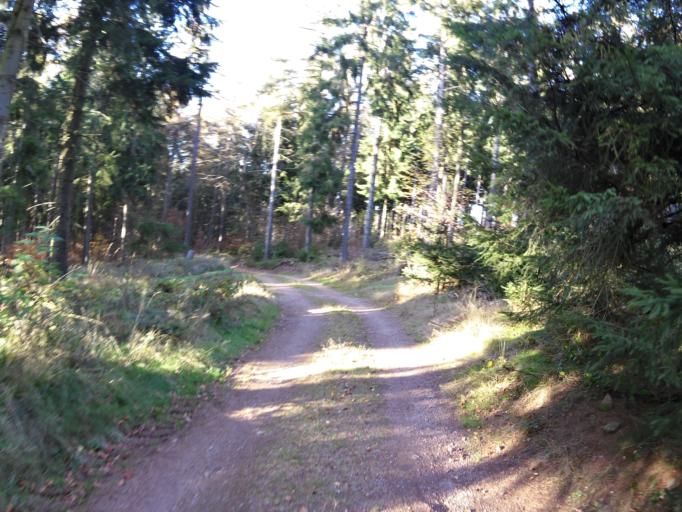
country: DE
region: Thuringia
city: Ruhla
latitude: 50.8688
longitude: 10.4038
